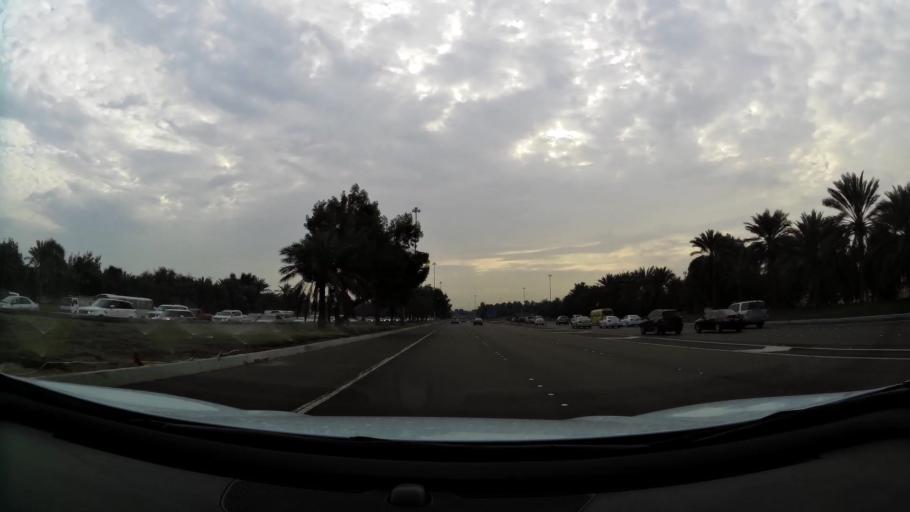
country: AE
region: Abu Dhabi
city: Abu Dhabi
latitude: 24.3945
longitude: 54.5180
